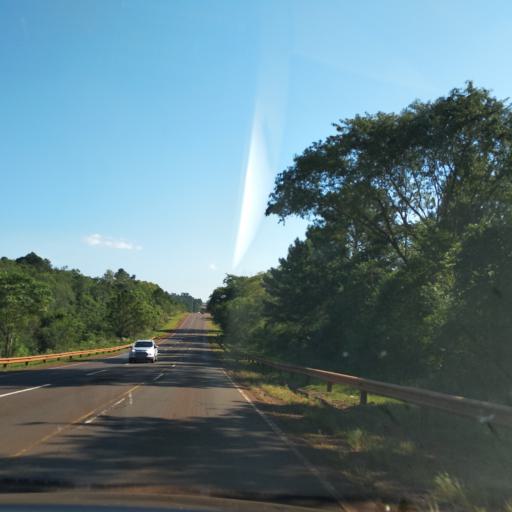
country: AR
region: Misiones
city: Jardin America
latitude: -27.0881
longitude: -55.2920
